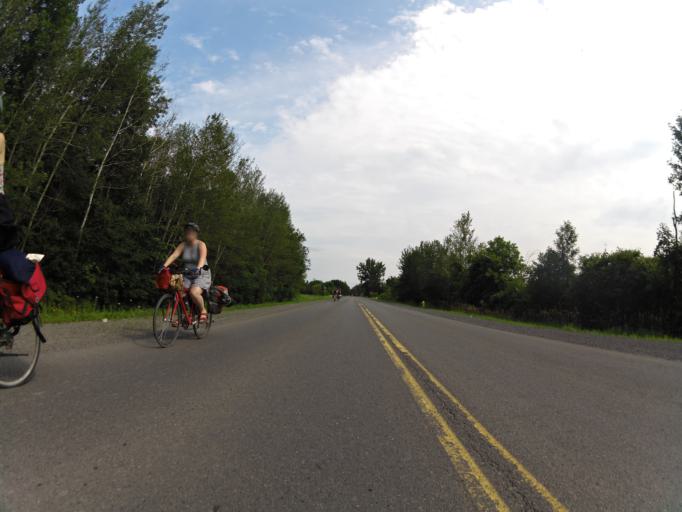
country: CA
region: Ontario
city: Prescott
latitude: 45.0234
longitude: -75.6338
